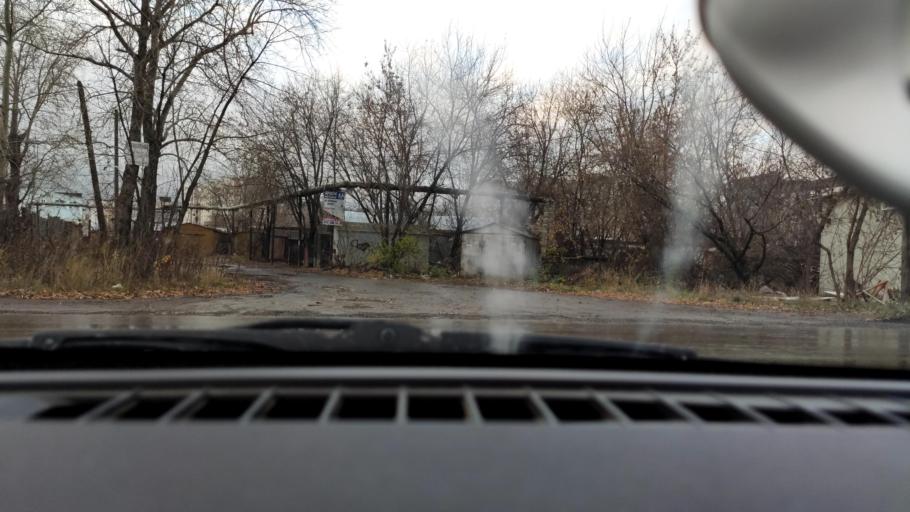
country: RU
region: Perm
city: Perm
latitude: 57.9695
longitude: 56.2330
